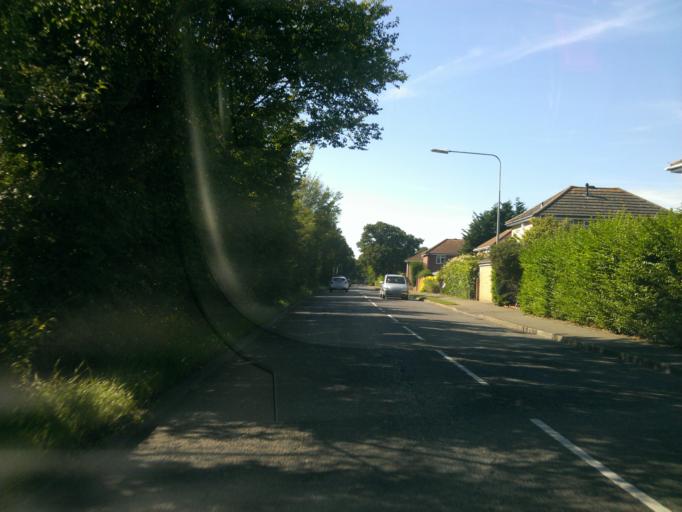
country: GB
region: England
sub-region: Essex
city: Layer de la Haye
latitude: 51.8618
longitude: 0.8787
